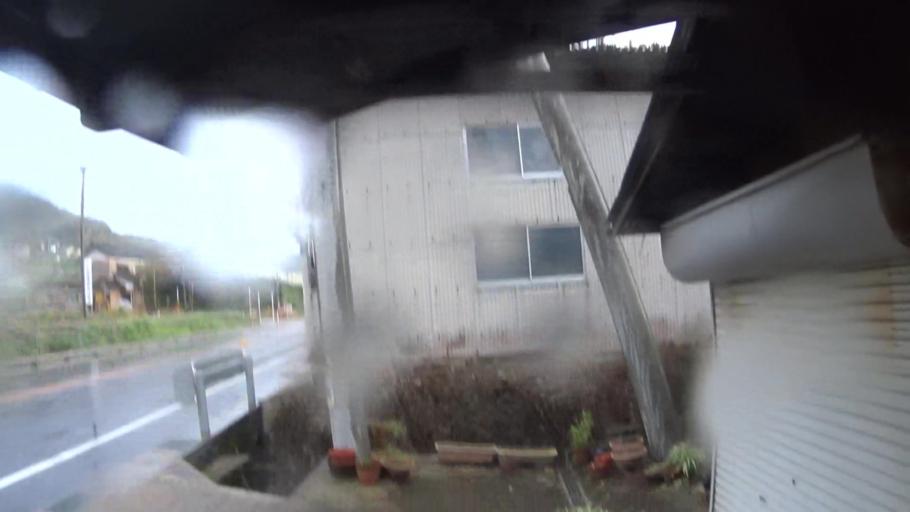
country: JP
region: Kyoto
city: Miyazu
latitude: 35.5454
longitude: 135.2106
